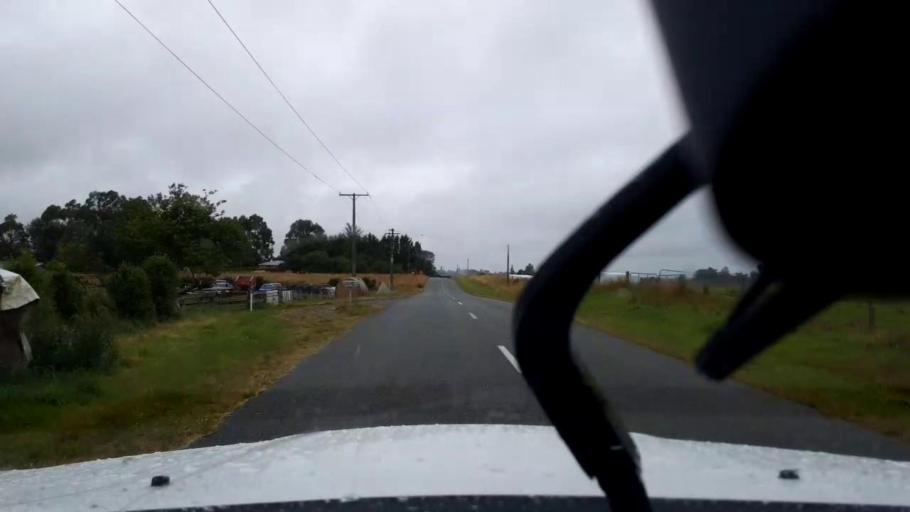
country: NZ
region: Canterbury
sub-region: Timaru District
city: Pleasant Point
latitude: -44.2512
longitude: 171.2310
